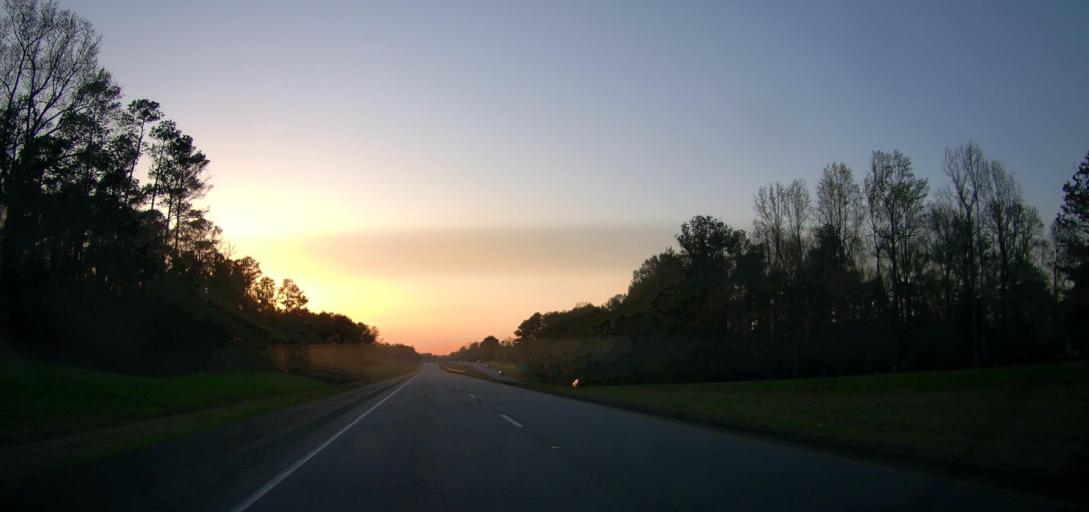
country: US
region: Alabama
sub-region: Coosa County
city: Goodwater
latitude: 32.9767
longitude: -86.0430
